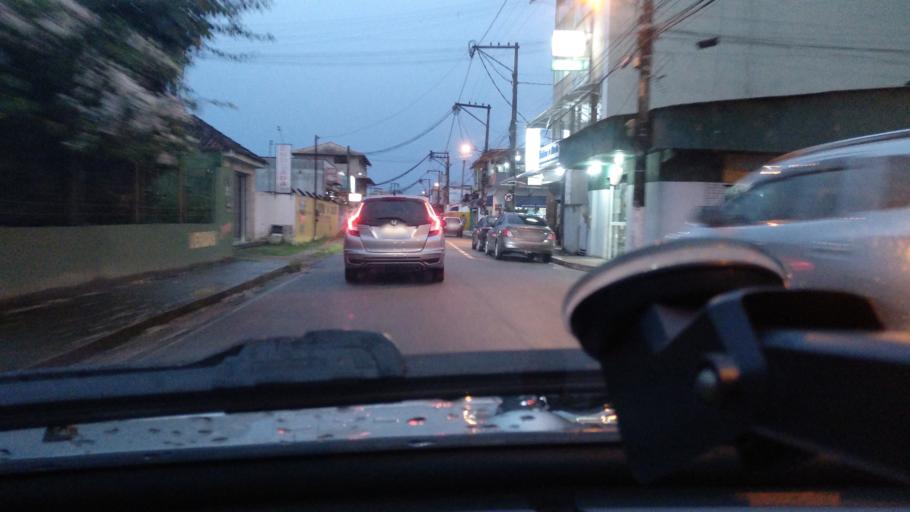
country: BR
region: Rio de Janeiro
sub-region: Angra Dos Reis
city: Angra dos Reis
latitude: -23.0138
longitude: -44.5370
